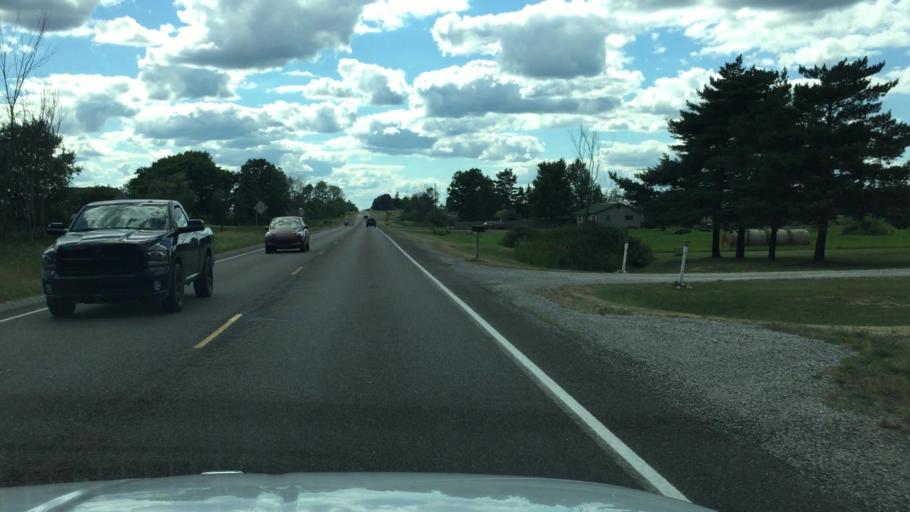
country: US
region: Michigan
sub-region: Saint Clair County
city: Capac
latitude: 43.0270
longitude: -82.9438
